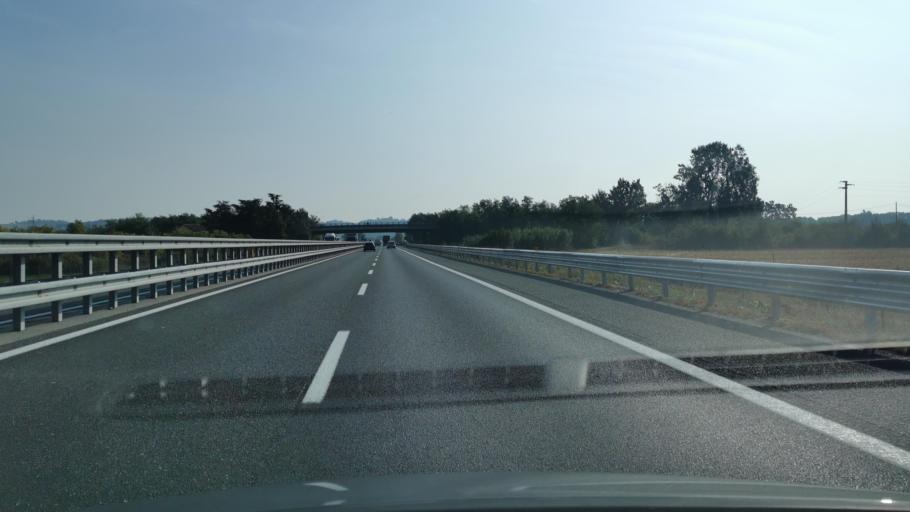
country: IT
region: Piedmont
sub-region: Provincia di Alessandria
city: Valle San Bartolomeo
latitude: 44.9436
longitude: 8.6190
